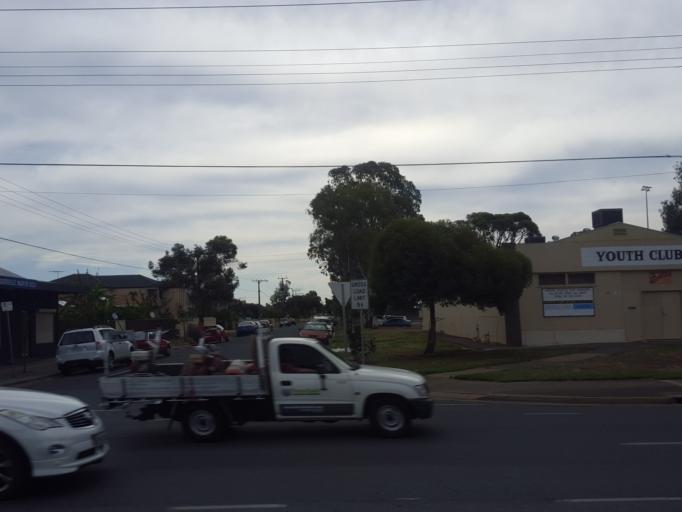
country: AU
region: South Australia
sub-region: Charles Sturt
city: Woodville North
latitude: -34.8615
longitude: 138.5475
